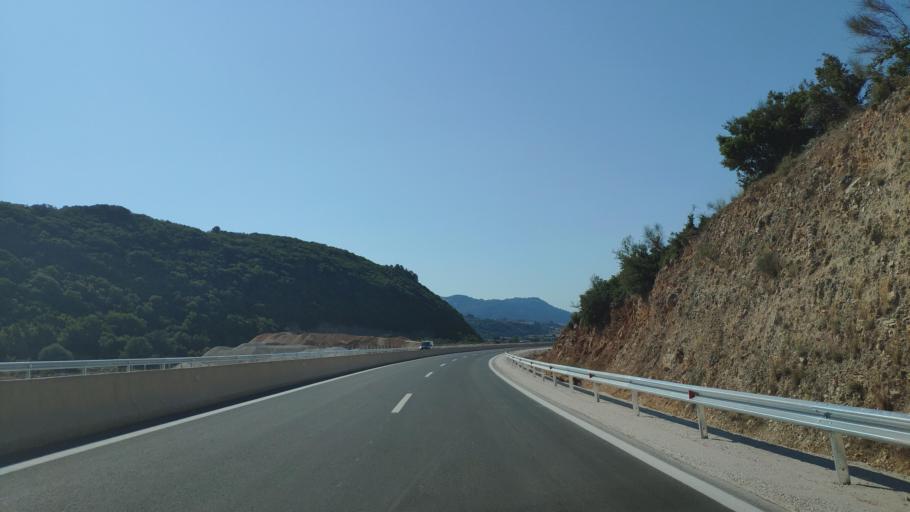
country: GR
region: West Greece
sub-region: Nomos Aitolias kai Akarnanias
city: Stanos
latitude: 38.7811
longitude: 21.1462
